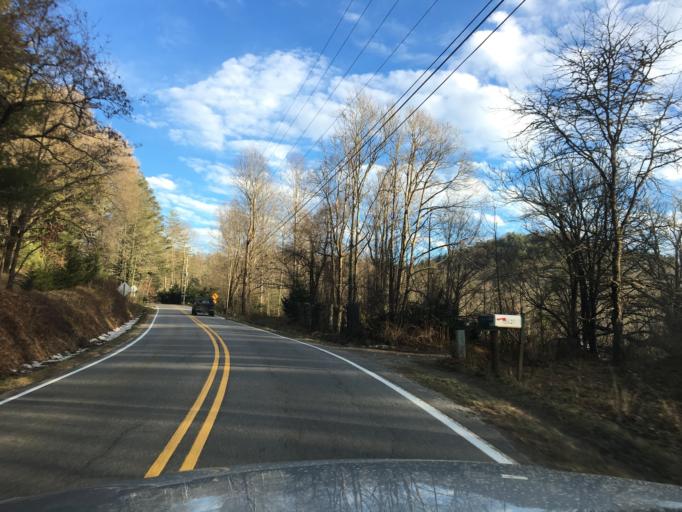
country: US
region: North Carolina
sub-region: Transylvania County
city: Brevard
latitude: 35.1104
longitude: -82.9709
